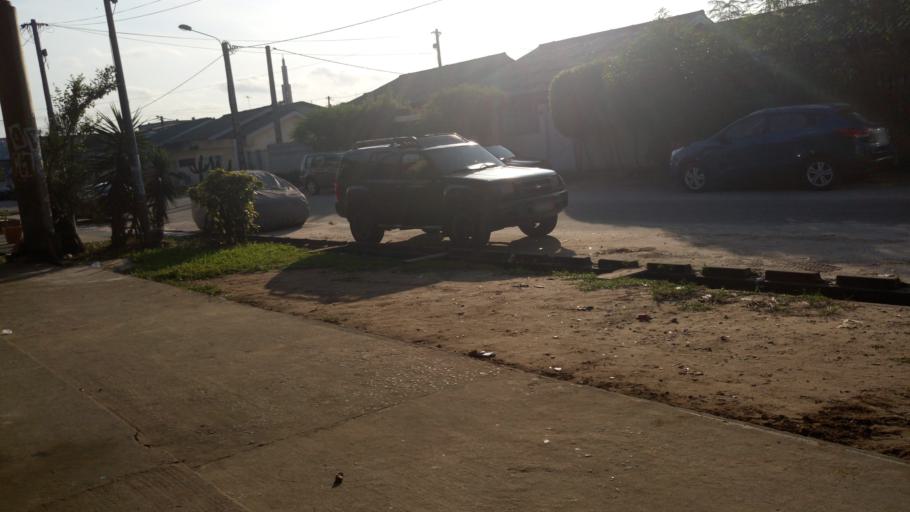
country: CI
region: Lagunes
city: Abobo
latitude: 5.4058
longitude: -3.9809
